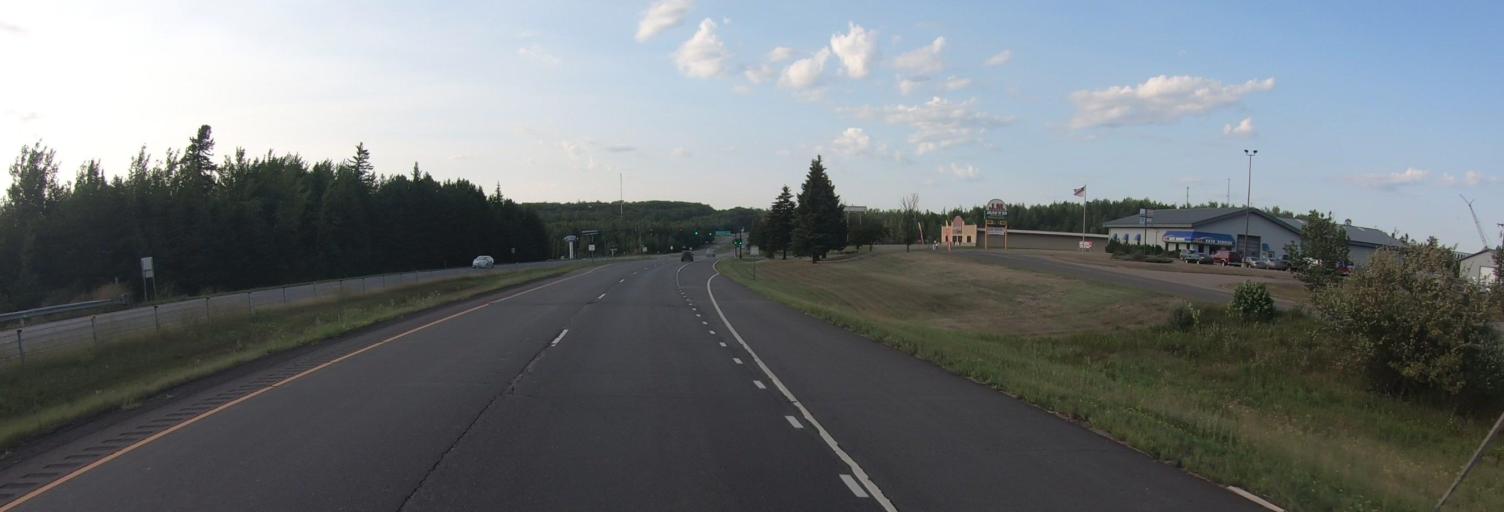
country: US
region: Minnesota
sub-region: Saint Louis County
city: Eveleth
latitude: 47.4757
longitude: -92.5298
